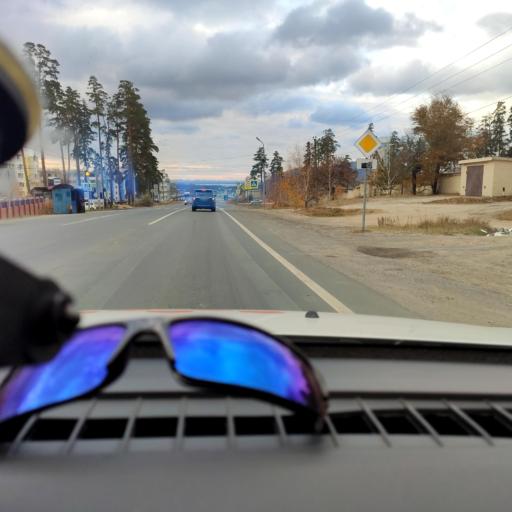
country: RU
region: Samara
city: Volzhskiy
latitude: 53.4388
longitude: 50.1242
